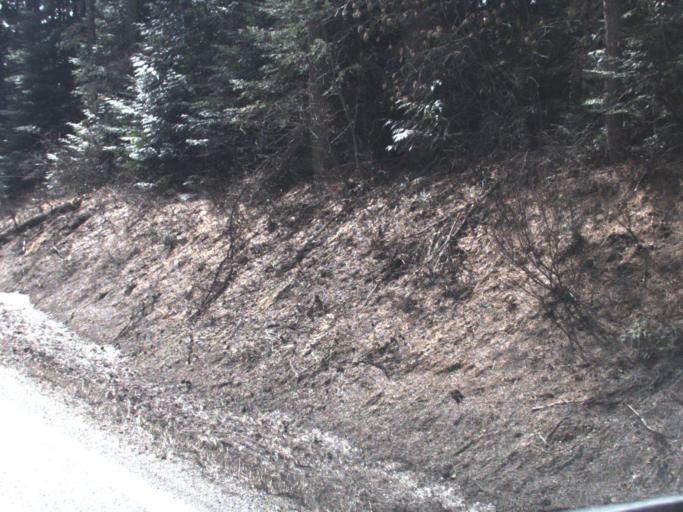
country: US
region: Washington
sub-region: Pend Oreille County
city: Newport
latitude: 48.4462
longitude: -117.3223
